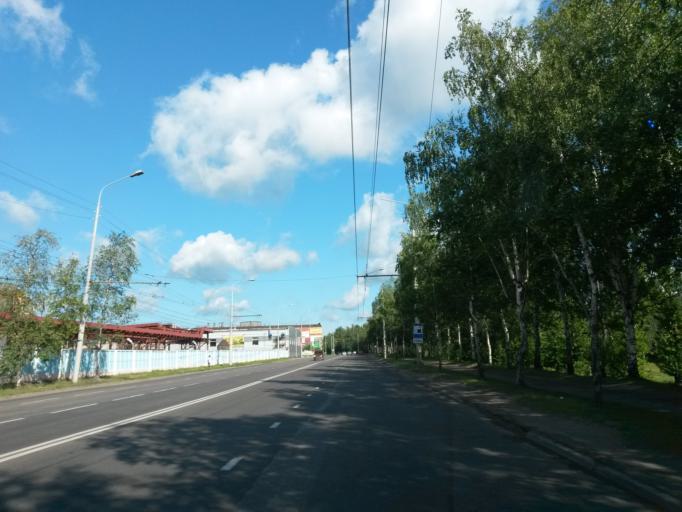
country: RU
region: Jaroslavl
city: Yaroslavl
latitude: 57.6492
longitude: 39.8778
